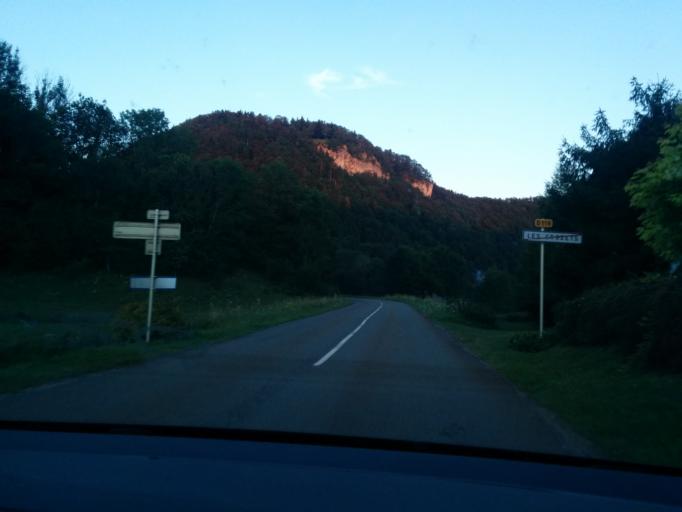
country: FR
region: Franche-Comte
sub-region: Departement du Jura
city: Saint-Lupicin
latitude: 46.4589
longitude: 5.7973
